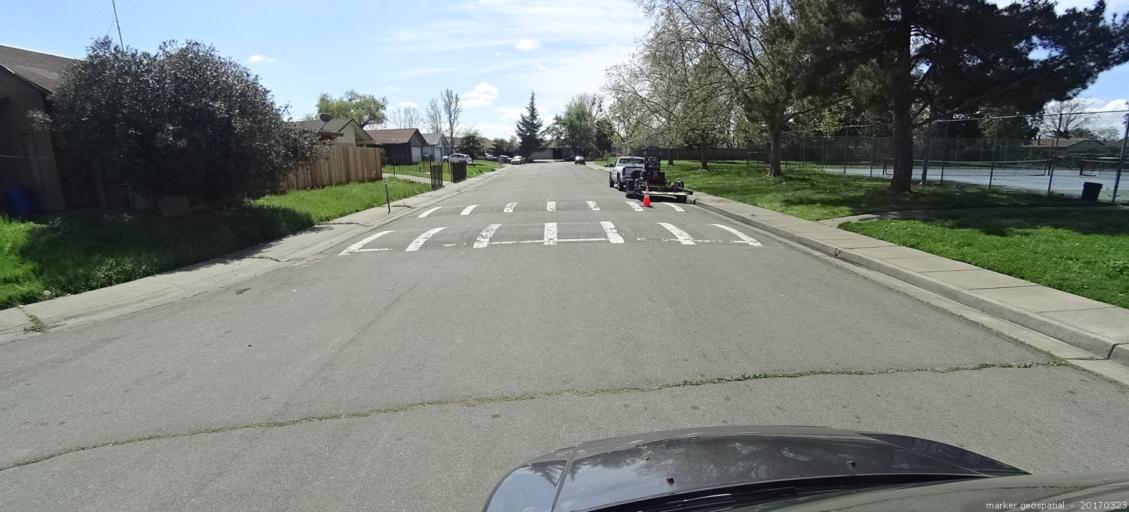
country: US
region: California
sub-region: Sacramento County
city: Florin
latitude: 38.5066
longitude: -121.4188
